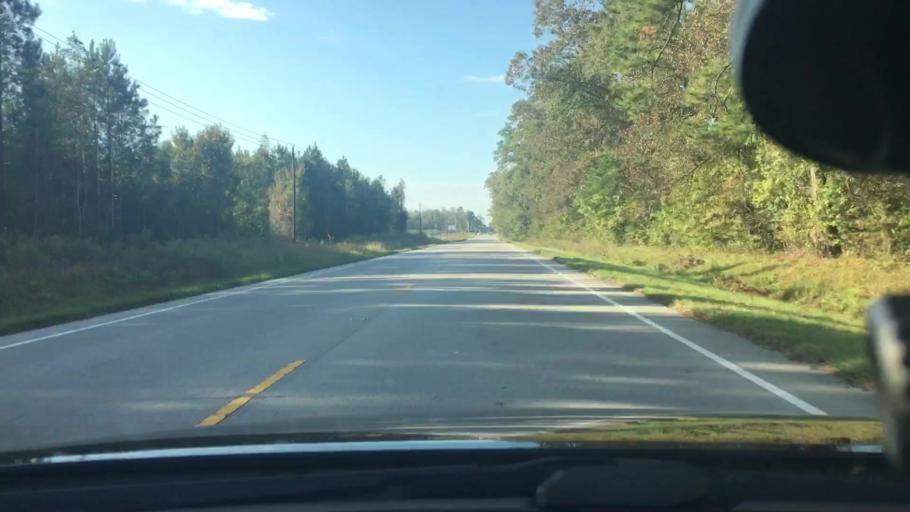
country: US
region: North Carolina
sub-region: Craven County
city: Vanceboro
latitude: 35.2449
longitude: -77.0836
